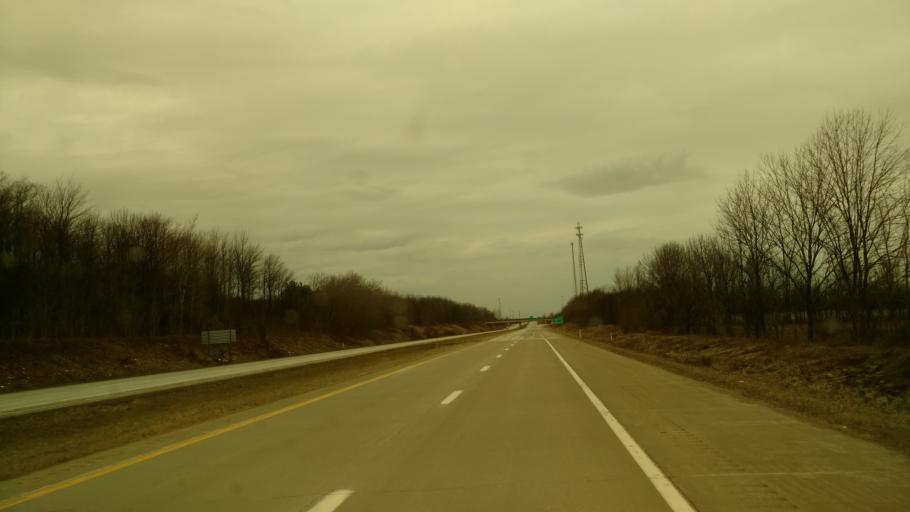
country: US
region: Pennsylvania
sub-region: Erie County
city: North East
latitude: 42.1520
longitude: -79.8769
